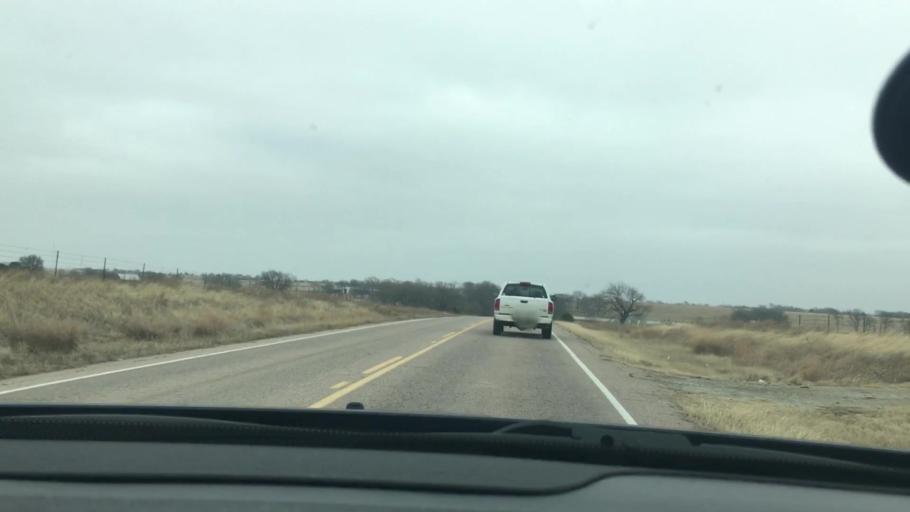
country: US
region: Oklahoma
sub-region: Marshall County
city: Madill
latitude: 34.1226
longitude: -96.7293
